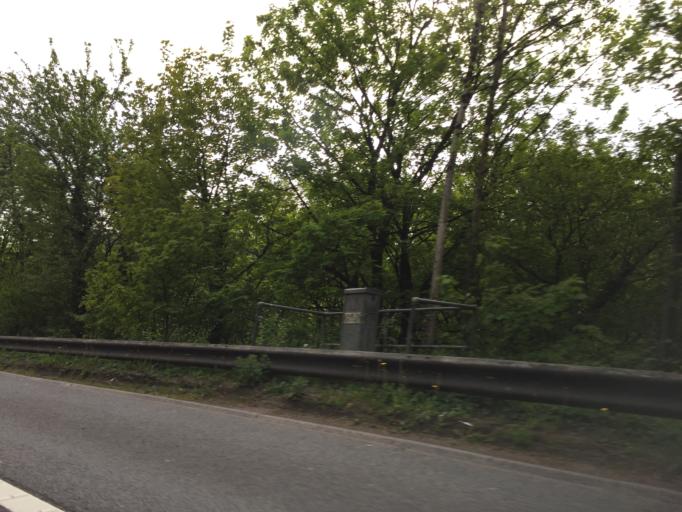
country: GB
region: Wales
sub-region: Cardiff
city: Pentyrch
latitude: 51.5563
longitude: -3.2700
